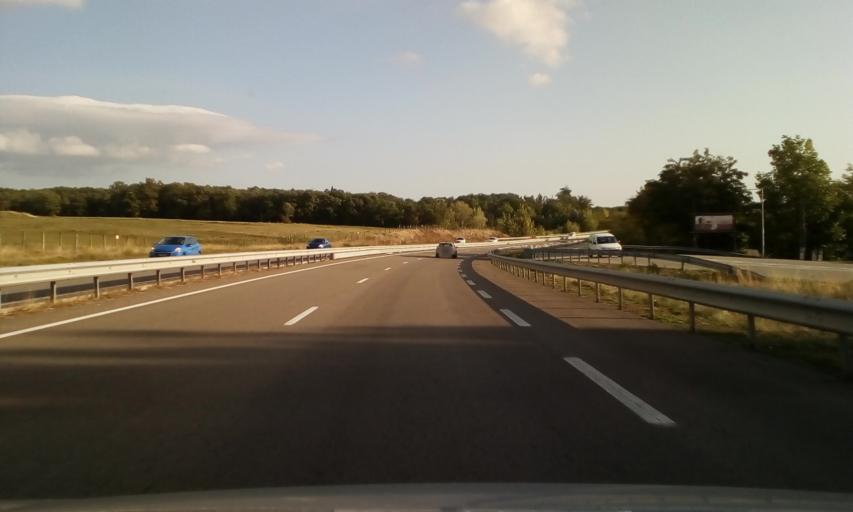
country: FR
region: Rhone-Alpes
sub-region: Departement de l'Ardeche
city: Davezieux
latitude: 45.2722
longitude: 4.7152
